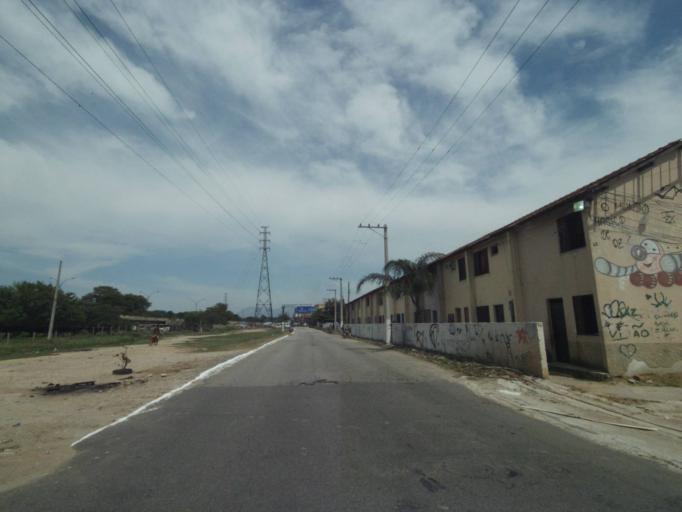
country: BR
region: Rio de Janeiro
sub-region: Duque De Caxias
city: Duque de Caxias
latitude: -22.7983
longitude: -43.3073
